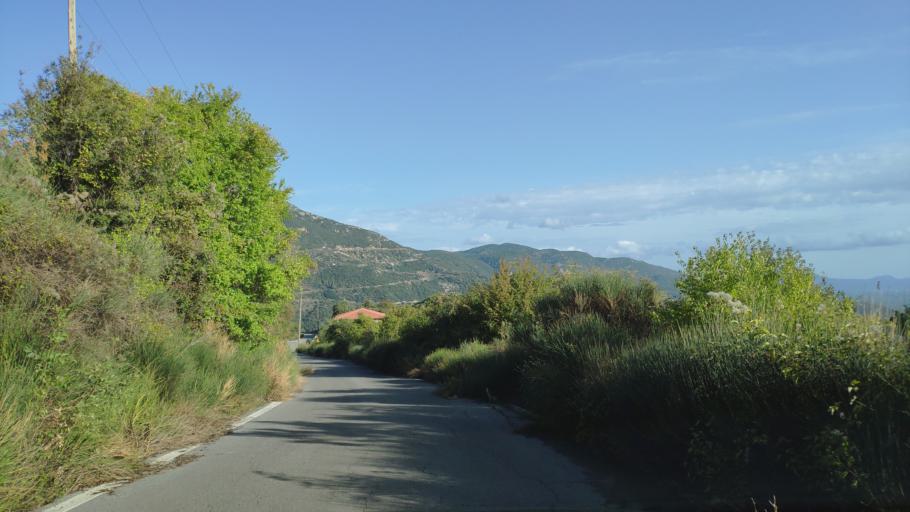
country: GR
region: Peloponnese
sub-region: Nomos Arkadias
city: Dimitsana
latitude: 37.5602
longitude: 22.0331
